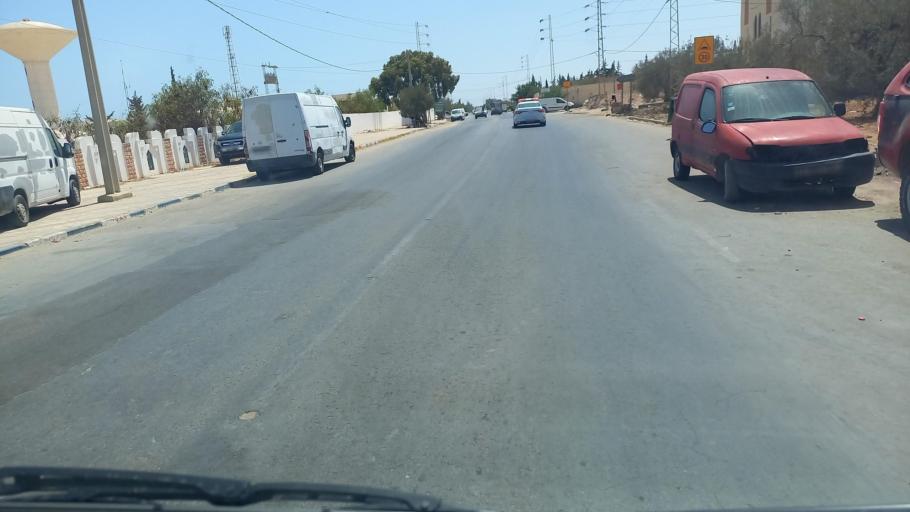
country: TN
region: Madanin
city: Zarzis
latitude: 33.5410
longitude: 11.0773
